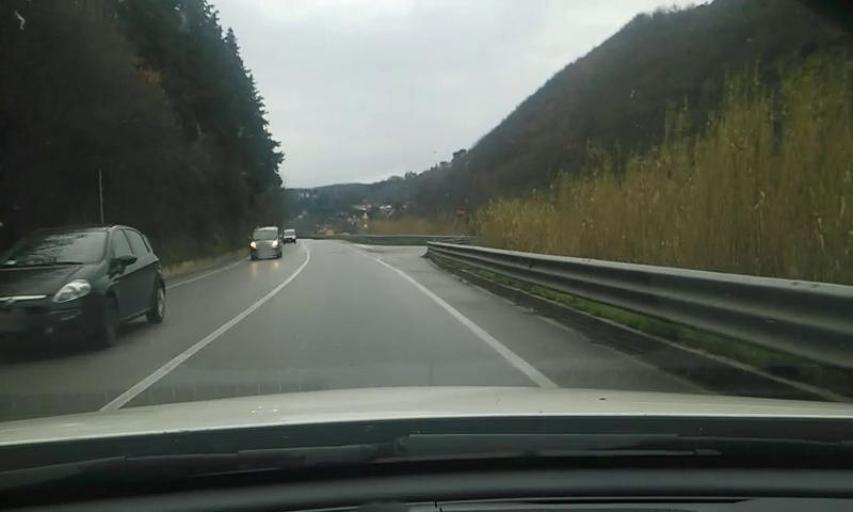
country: IT
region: Tuscany
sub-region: Provincia di Prato
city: Vaiano
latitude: 43.9182
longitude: 11.1259
